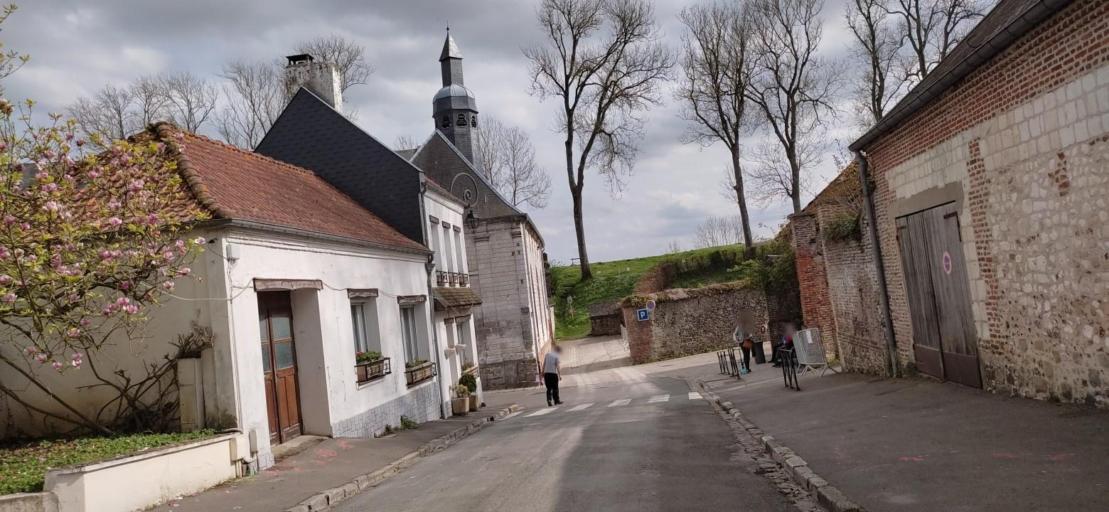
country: FR
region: Nord-Pas-de-Calais
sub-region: Departement du Pas-de-Calais
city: Montreuil
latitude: 50.4628
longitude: 1.7641
